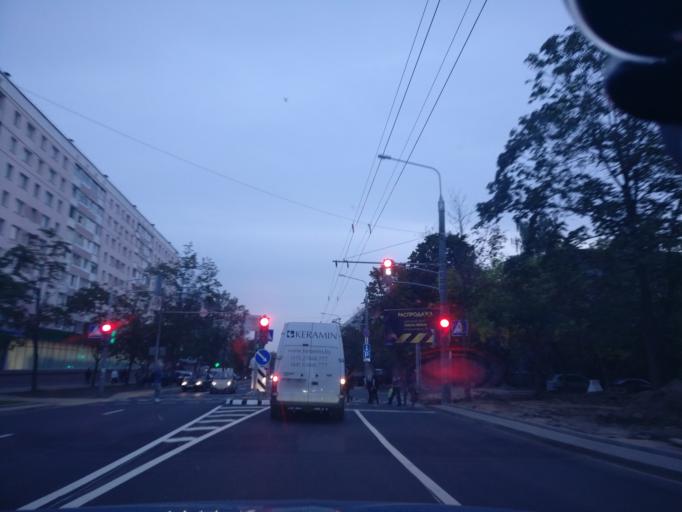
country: BY
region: Minsk
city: Minsk
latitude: 53.9253
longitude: 27.5819
